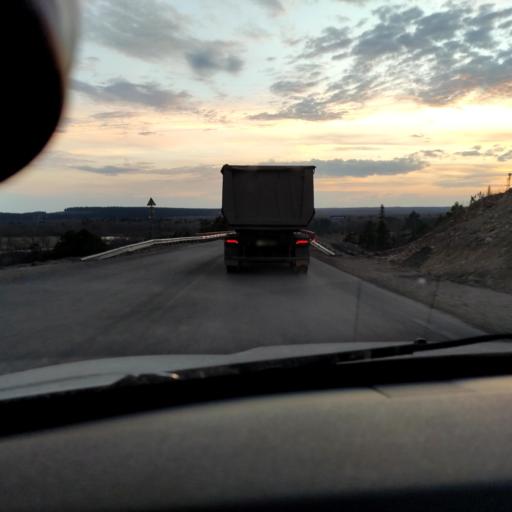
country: RU
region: Perm
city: Chusovoy
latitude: 58.3298
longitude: 57.7880
